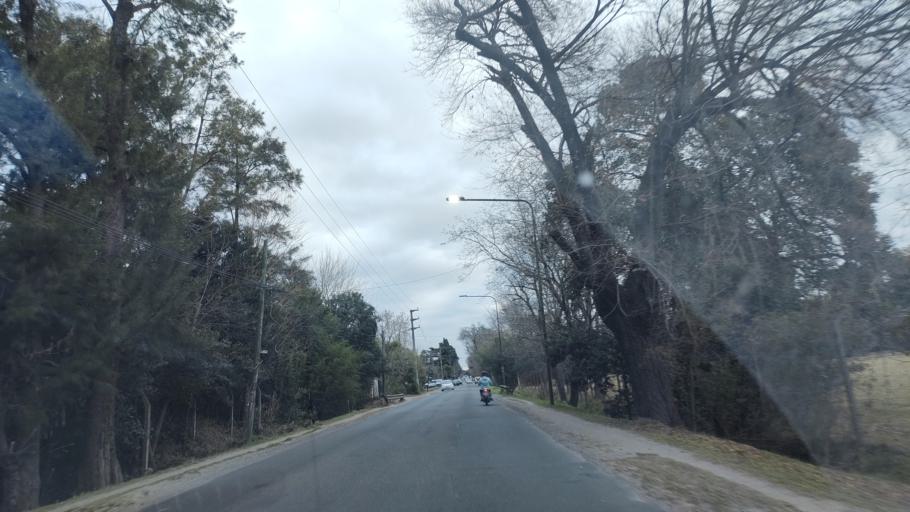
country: AR
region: Buenos Aires
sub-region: Partido de La Plata
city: La Plata
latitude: -34.8655
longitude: -58.0931
